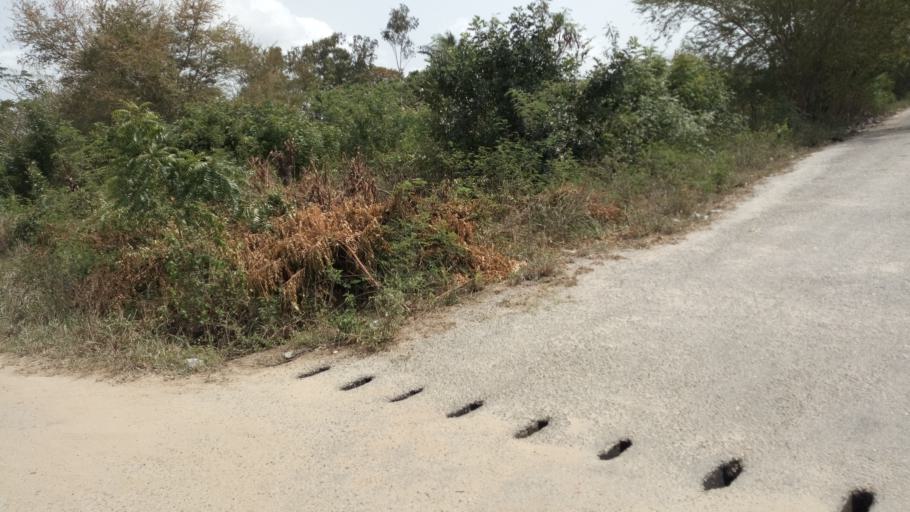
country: GH
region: Central
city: Winneba
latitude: 5.3667
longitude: -0.6466
